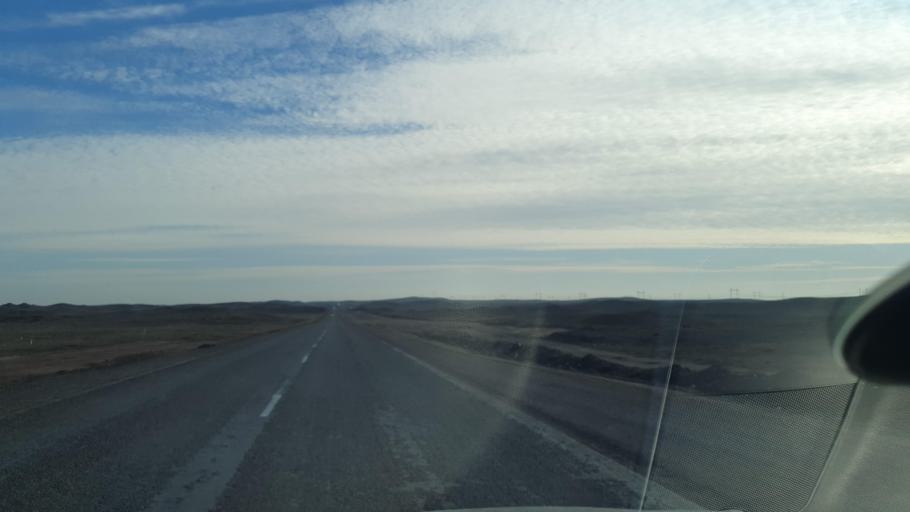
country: KZ
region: Zhambyl
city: Mynaral
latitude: 45.5344
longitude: 73.4761
